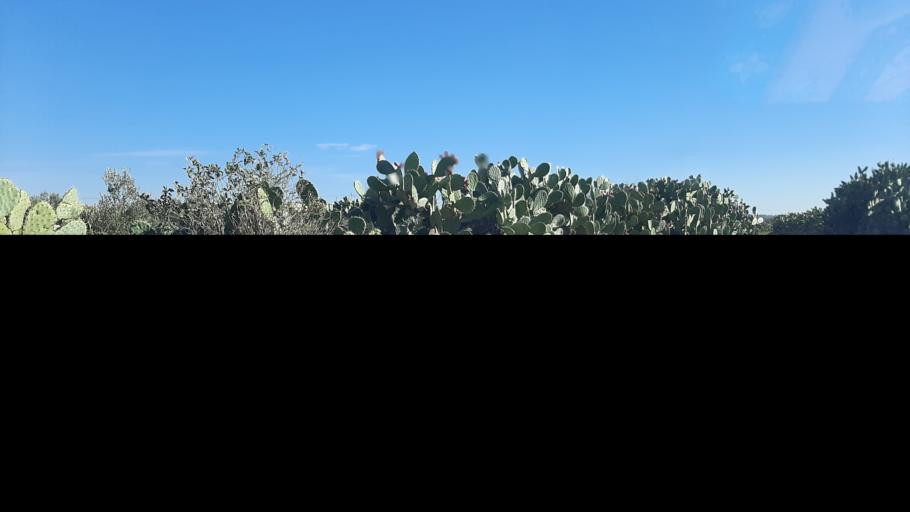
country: TN
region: Safaqis
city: Bi'r `Ali Bin Khalifah
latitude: 35.0266
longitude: 10.0767
